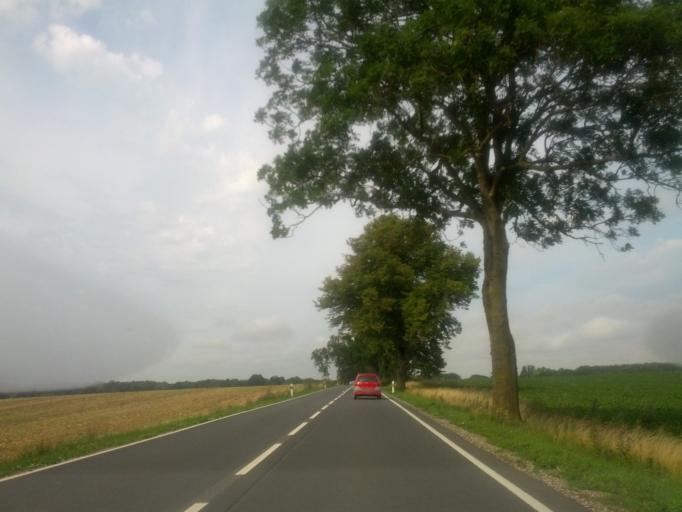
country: DE
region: Mecklenburg-Vorpommern
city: Sellin
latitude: 53.9306
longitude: 11.6029
